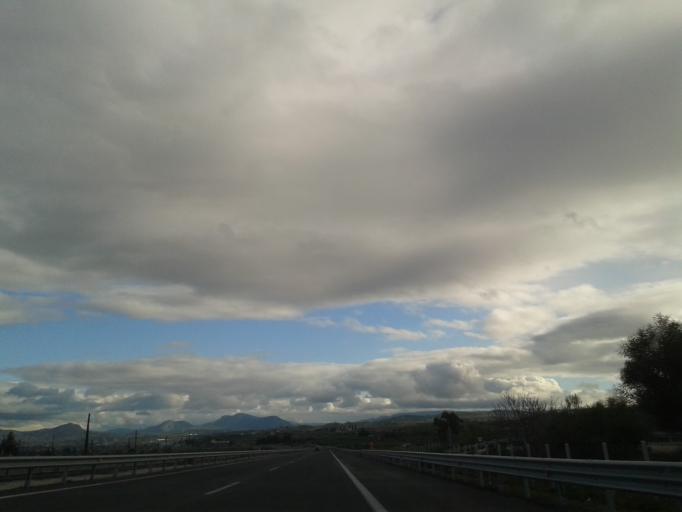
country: GR
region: Peloponnese
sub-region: Nomos Korinthias
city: Velo
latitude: 37.9518
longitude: 22.7538
